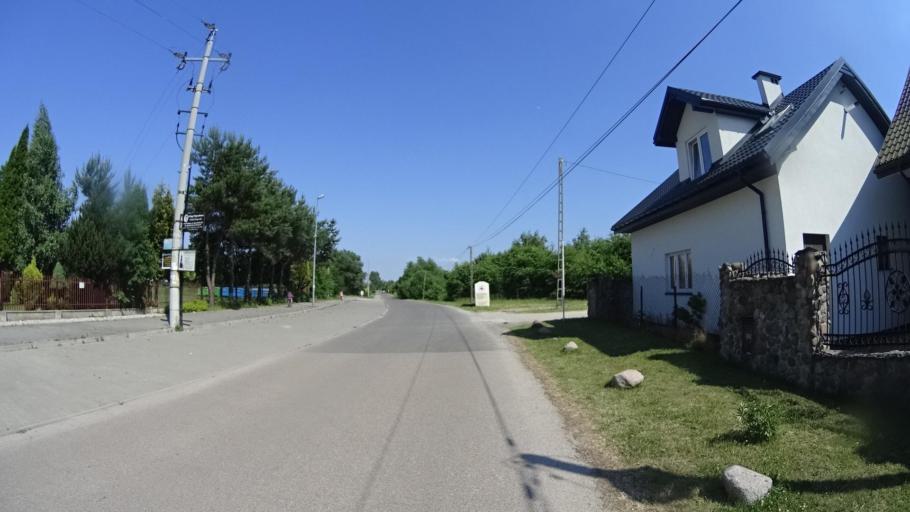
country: PL
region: Masovian Voivodeship
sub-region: Powiat warszawski zachodni
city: Bieniewice
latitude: 52.1920
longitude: 20.5316
